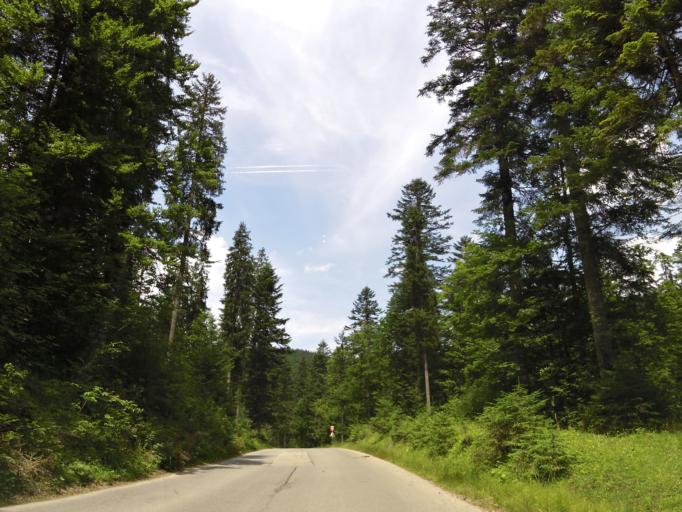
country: AT
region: Tyrol
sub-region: Politischer Bezirk Kitzbuhel
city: Waidring
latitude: 47.6609
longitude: 12.5696
